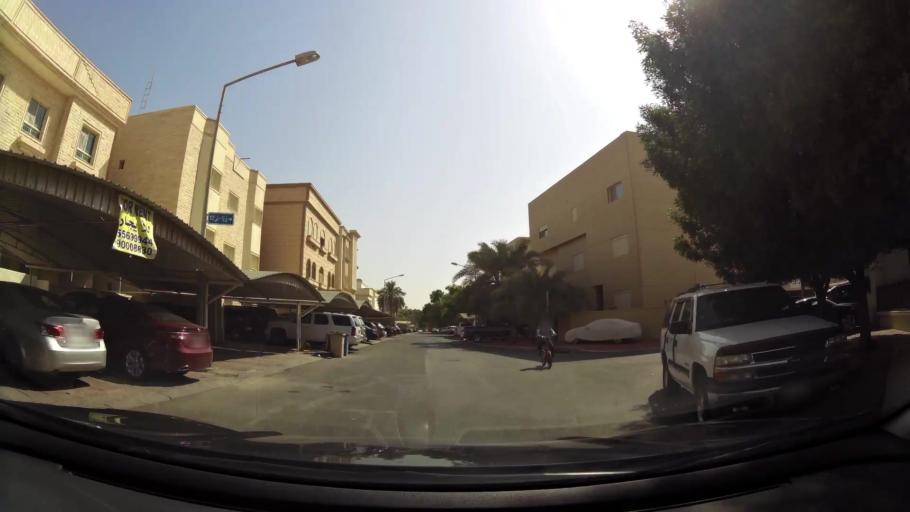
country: KW
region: Muhafazat Hawalli
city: Salwa
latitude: 29.2780
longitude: 48.0860
